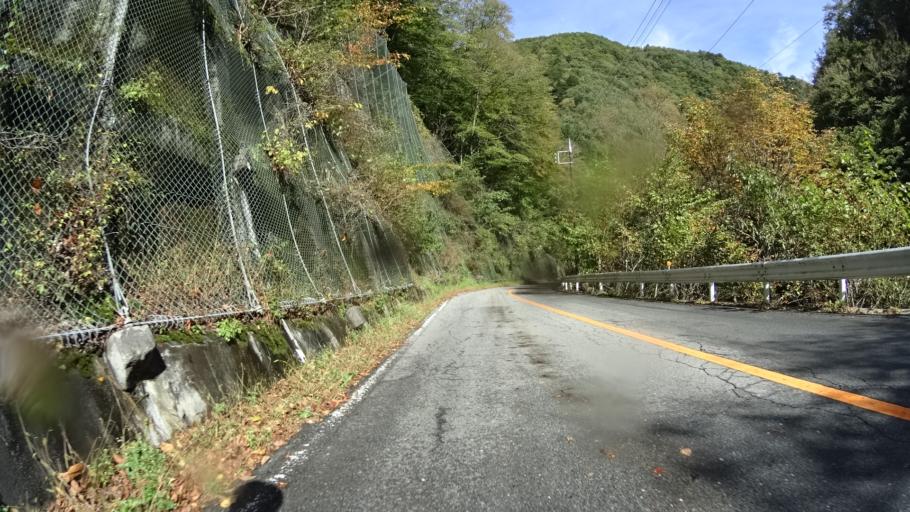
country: JP
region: Yamanashi
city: Enzan
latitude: 35.8044
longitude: 138.8451
